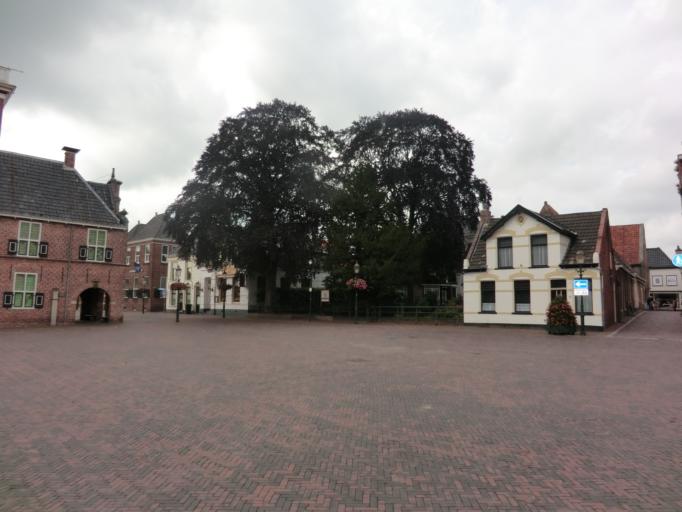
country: NL
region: Groningen
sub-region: Gemeente Appingedam
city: Appingedam
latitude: 53.3200
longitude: 6.8581
